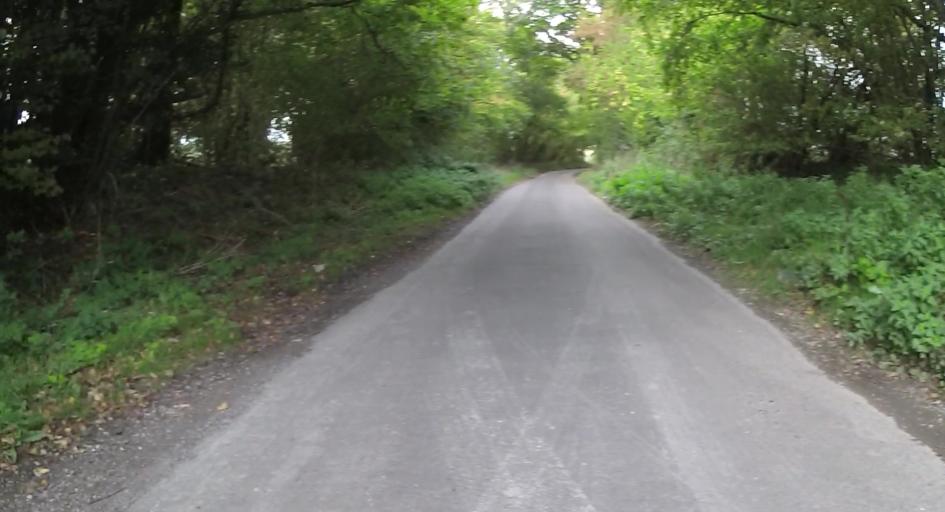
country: GB
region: England
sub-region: Hampshire
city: Alton
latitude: 51.1604
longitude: -0.9273
